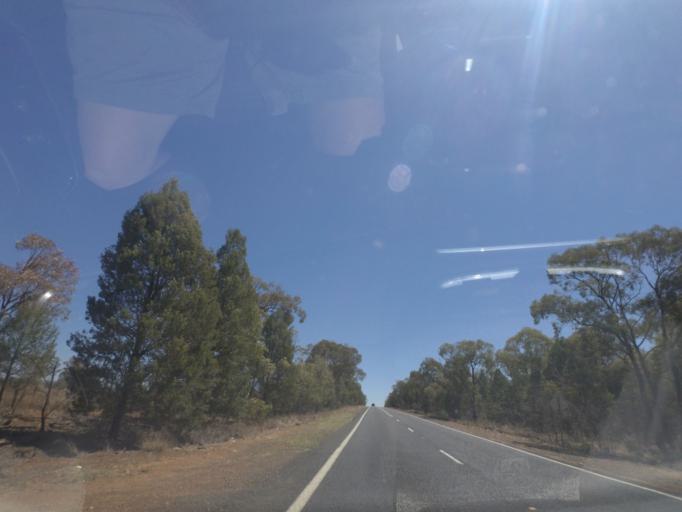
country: AU
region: New South Wales
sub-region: Gilgandra
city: Gilgandra
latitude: -31.4736
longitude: 148.9002
